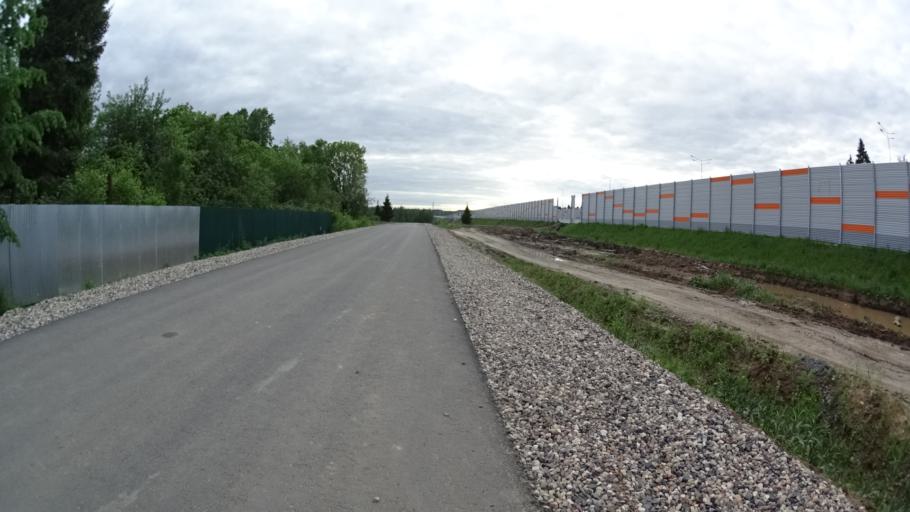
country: RU
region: Moskovskaya
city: Zelenogradskiy
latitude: 56.1252
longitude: 37.9062
